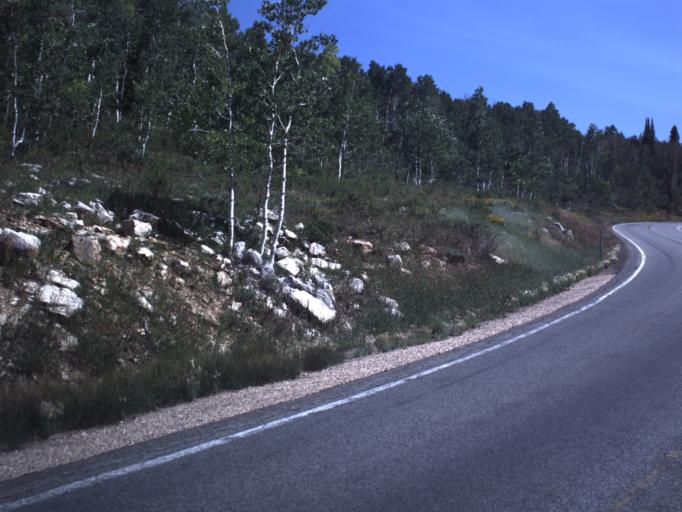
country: US
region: Utah
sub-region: Sanpete County
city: Fairview
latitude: 39.6765
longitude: -111.3207
